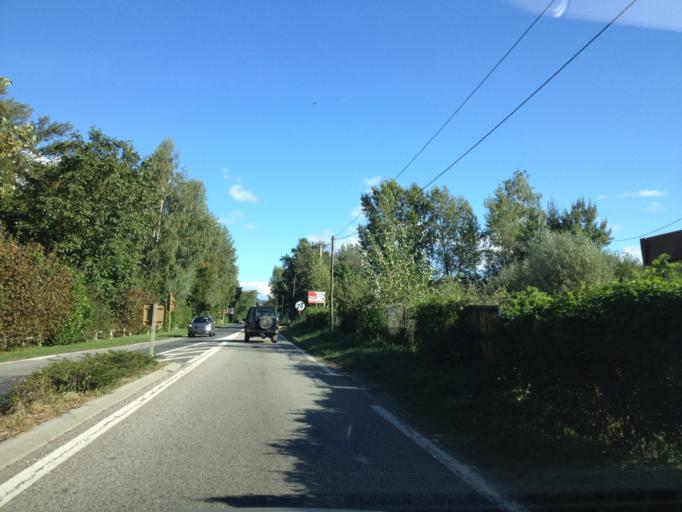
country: FR
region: Rhone-Alpes
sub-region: Departement de la Savoie
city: Le Bourget-du-Lac
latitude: 45.6411
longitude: 5.8660
